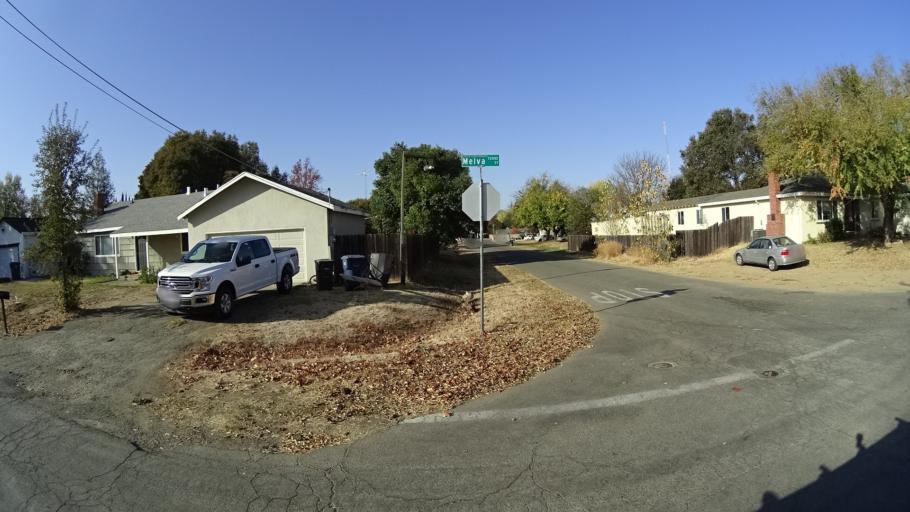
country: US
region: California
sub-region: Sacramento County
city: Citrus Heights
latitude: 38.6971
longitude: -121.2542
